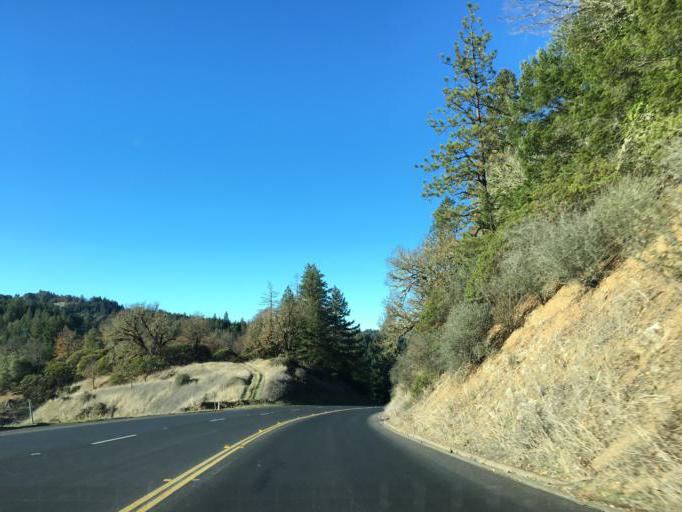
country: US
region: California
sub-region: Mendocino County
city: Laytonville
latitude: 39.7594
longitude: -123.5390
